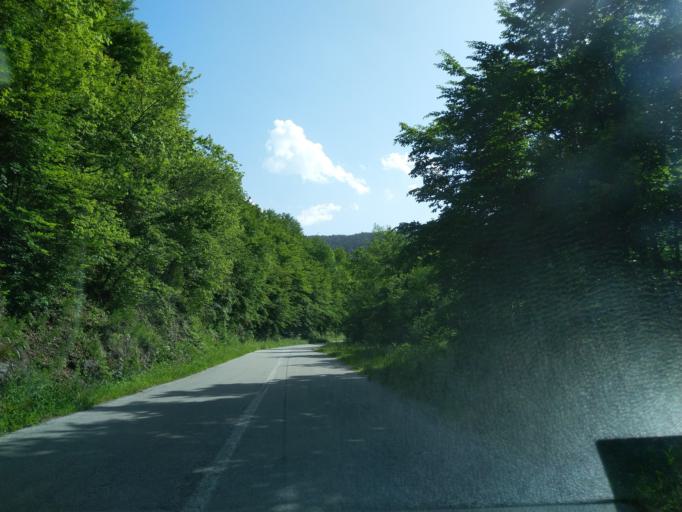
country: RS
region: Central Serbia
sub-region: Zlatiborski Okrug
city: Bajina Basta
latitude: 43.8613
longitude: 19.6254
